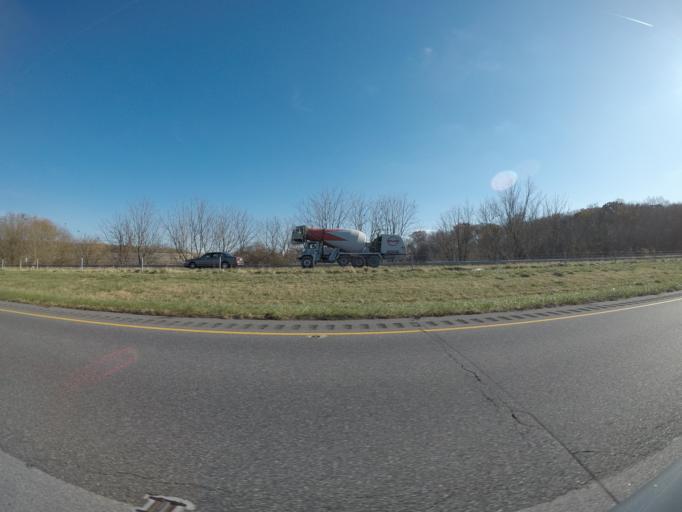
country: US
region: Pennsylvania
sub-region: Chester County
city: Oxford
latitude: 39.7971
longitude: -75.9852
